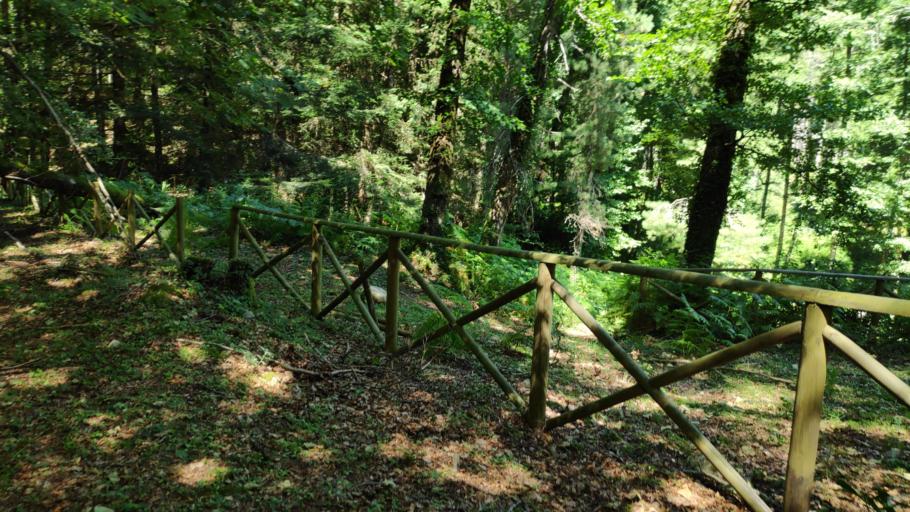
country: IT
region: Calabria
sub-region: Provincia di Vibo-Valentia
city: Nardodipace
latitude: 38.5027
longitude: 16.3757
